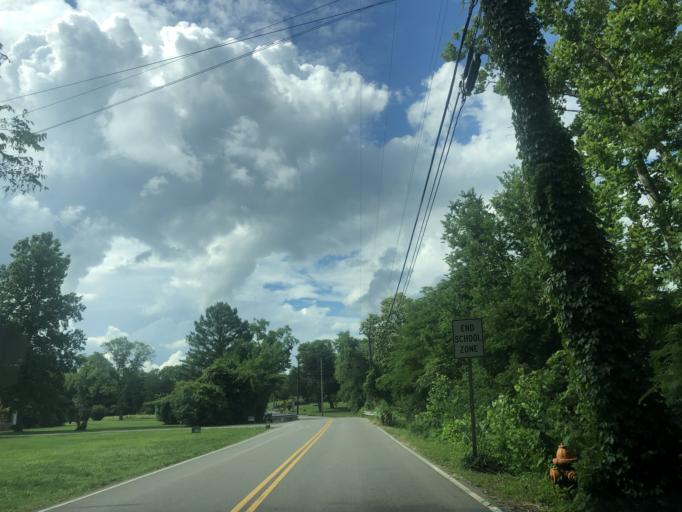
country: US
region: Tennessee
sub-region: Davidson County
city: Nashville
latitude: 36.2133
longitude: -86.8664
